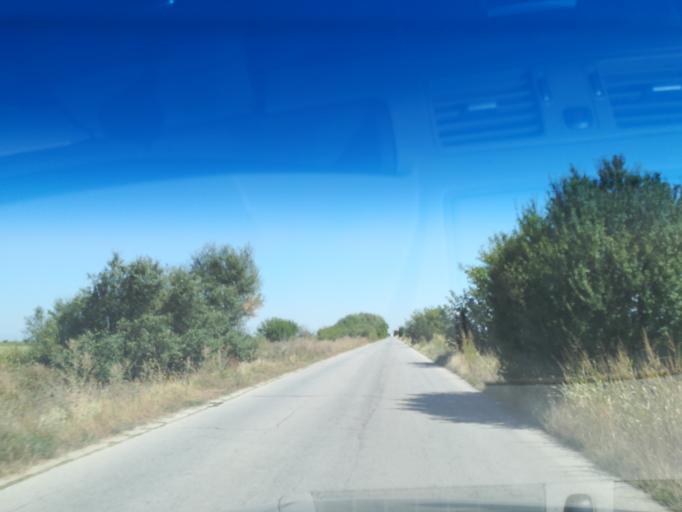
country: BG
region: Plovdiv
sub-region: Obshtina Suedinenie
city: Suedinenie
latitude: 42.2514
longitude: 24.4700
